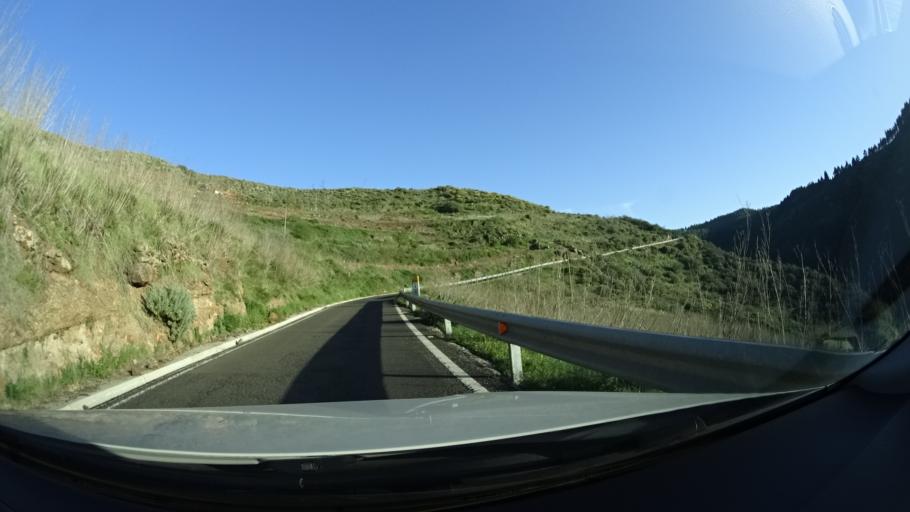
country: ES
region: Canary Islands
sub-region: Provincia de Las Palmas
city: Artenara
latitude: 28.0372
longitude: -15.6721
